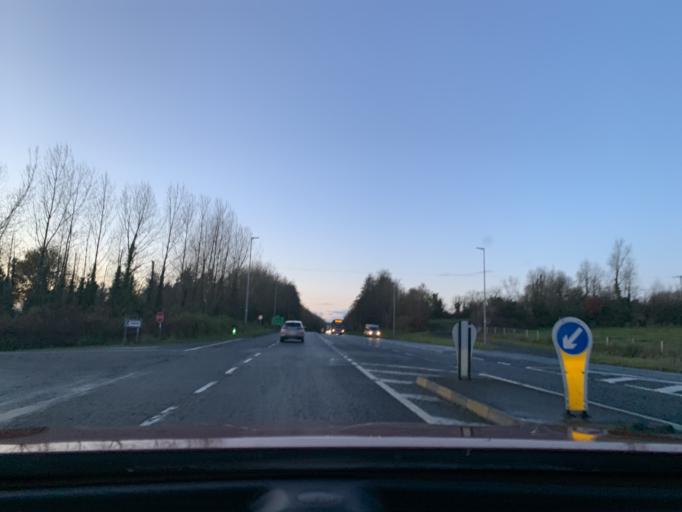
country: IE
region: Connaught
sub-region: County Leitrim
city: Carrick-on-Shannon
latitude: 53.9192
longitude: -7.9854
